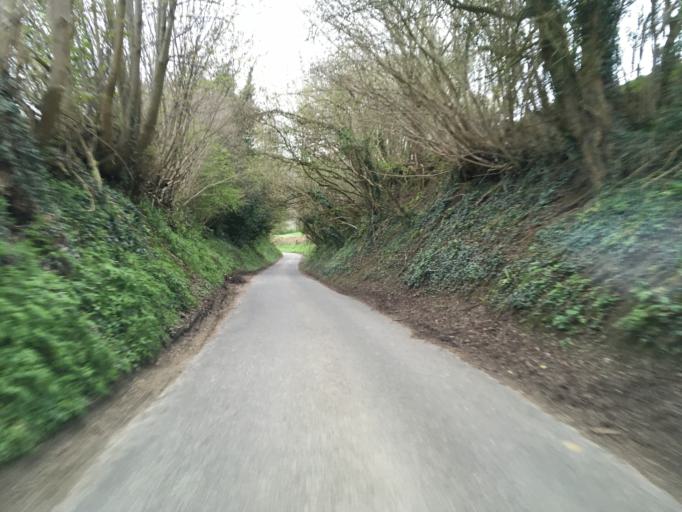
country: GB
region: England
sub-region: Gloucestershire
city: Wotton-under-Edge
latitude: 51.6061
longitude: -2.3240
